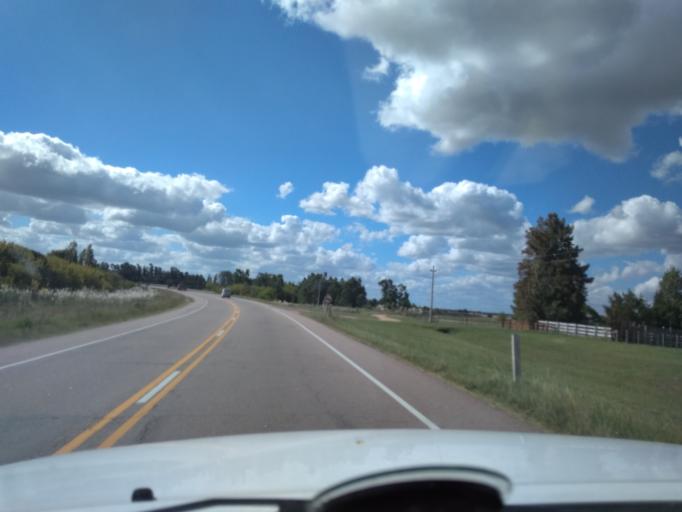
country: UY
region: Canelones
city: Sauce
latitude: -34.6758
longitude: -56.0512
